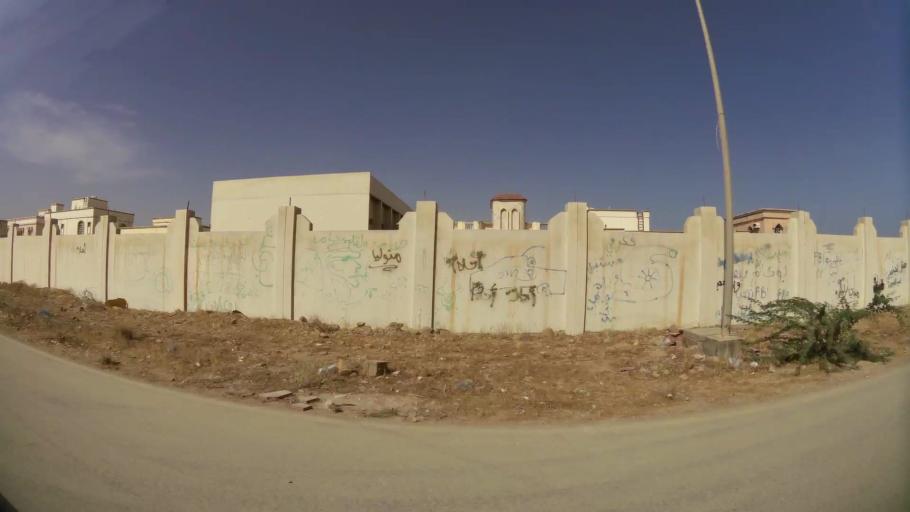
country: OM
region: Zufar
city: Salalah
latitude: 17.0006
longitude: 54.0097
